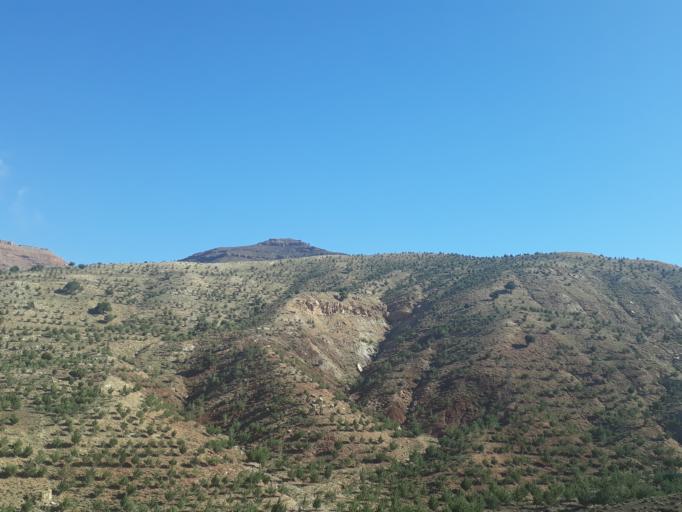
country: MA
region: Souss-Massa-Draa
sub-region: Ouarzazate
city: Telouet
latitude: 31.2614
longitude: -7.3934
